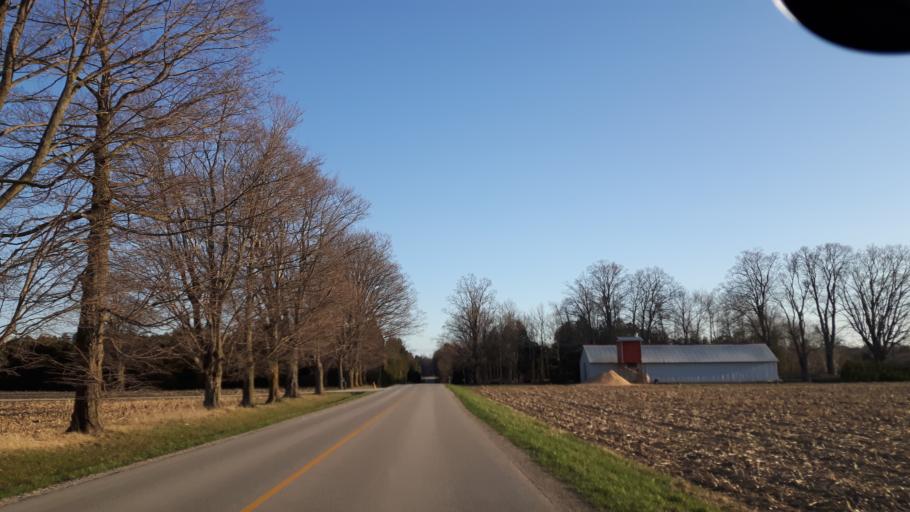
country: CA
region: Ontario
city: Goderich
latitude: 43.6158
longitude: -81.6847
